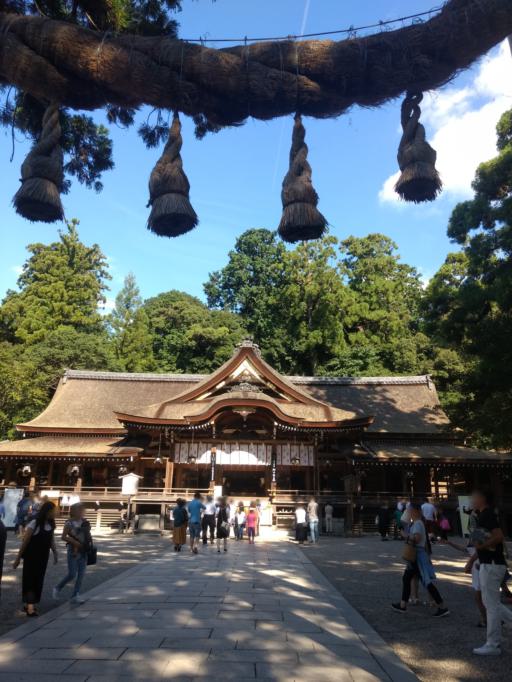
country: JP
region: Nara
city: Sakurai
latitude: 34.5284
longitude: 135.8527
